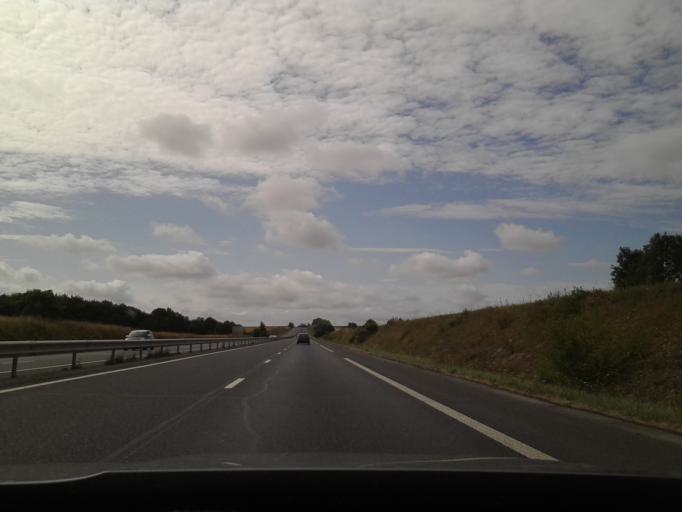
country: FR
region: Lower Normandy
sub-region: Departement du Calvados
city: Potigny
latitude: 48.9975
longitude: -0.2561
